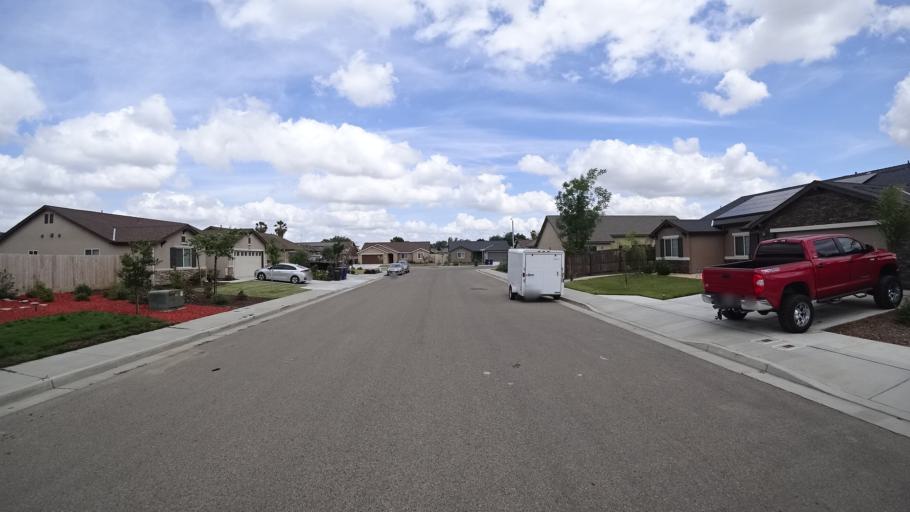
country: US
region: California
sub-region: Kings County
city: Home Garden
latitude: 36.3010
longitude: -119.6584
